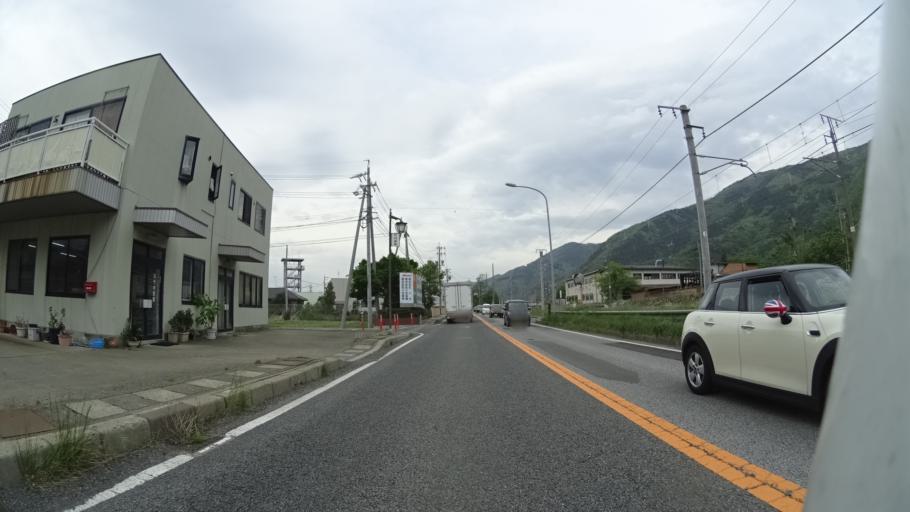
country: JP
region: Nagano
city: Ueda
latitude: 36.4769
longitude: 138.1581
